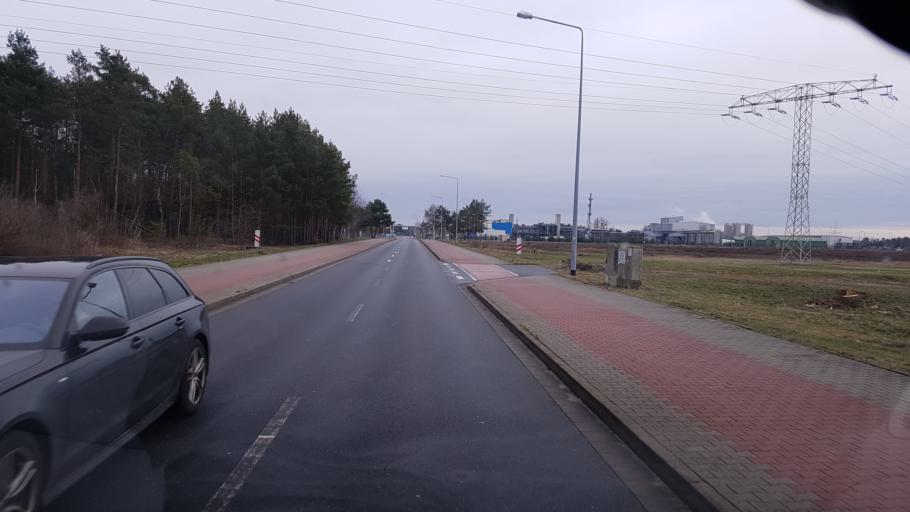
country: DE
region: Brandenburg
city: Ruhland
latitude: 51.4719
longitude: 13.8740
